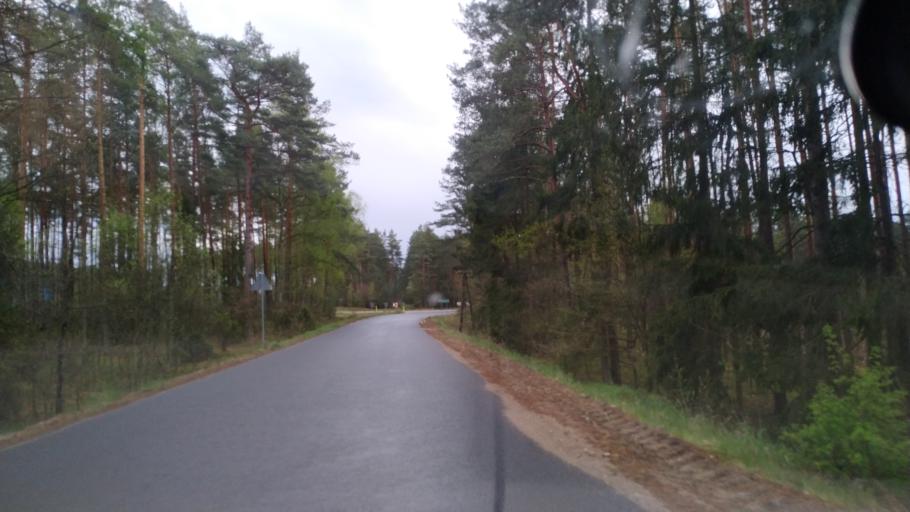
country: PL
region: Pomeranian Voivodeship
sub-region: Powiat starogardzki
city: Osiek
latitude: 53.6517
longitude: 18.4916
